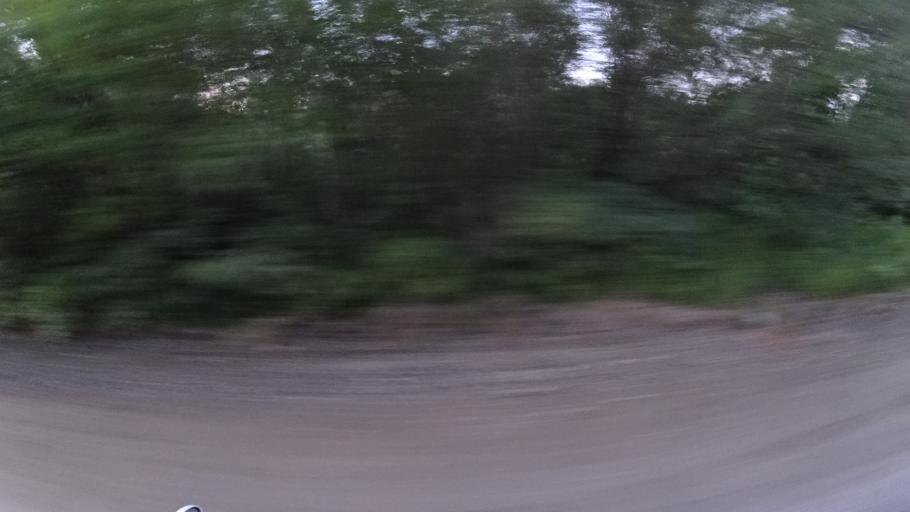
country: RU
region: Khabarovsk Krai
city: Khor
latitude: 47.8512
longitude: 134.9455
